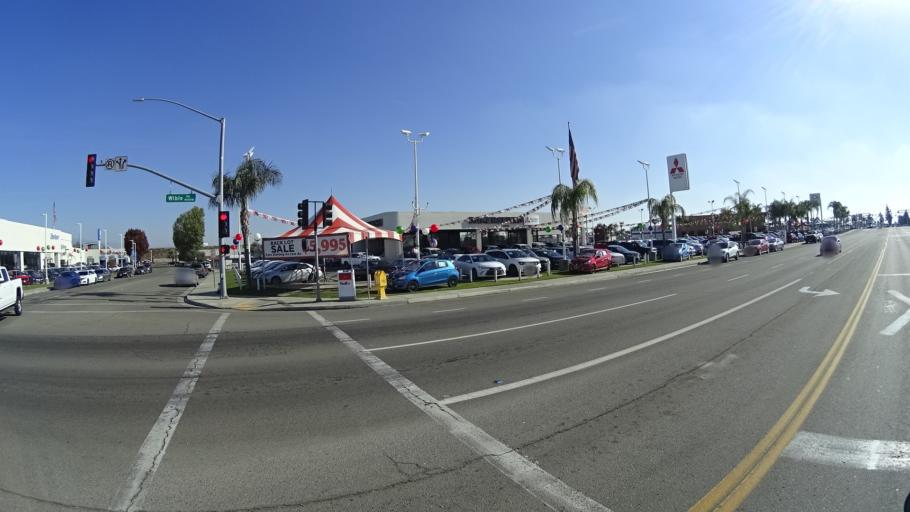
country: US
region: California
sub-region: Kern County
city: Greenfield
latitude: 35.3128
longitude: -119.0390
